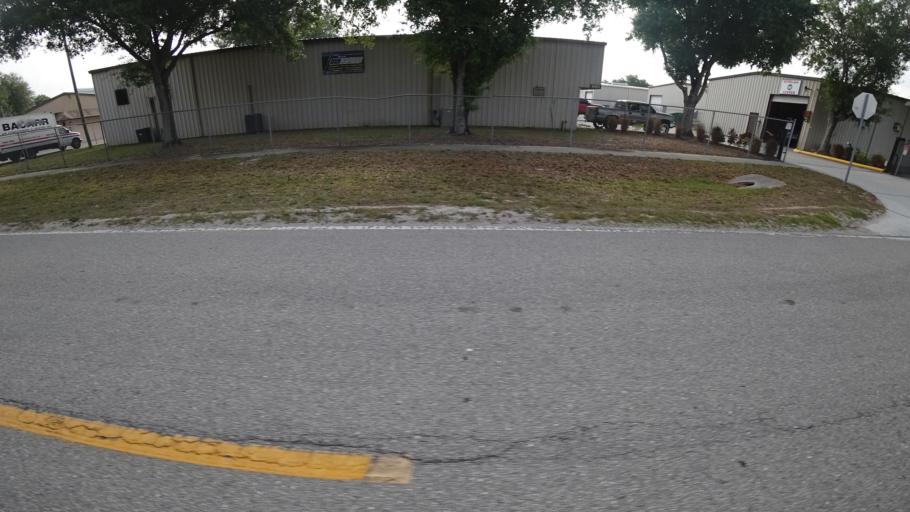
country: US
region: Florida
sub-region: Manatee County
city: Whitfield
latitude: 27.4223
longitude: -82.5219
